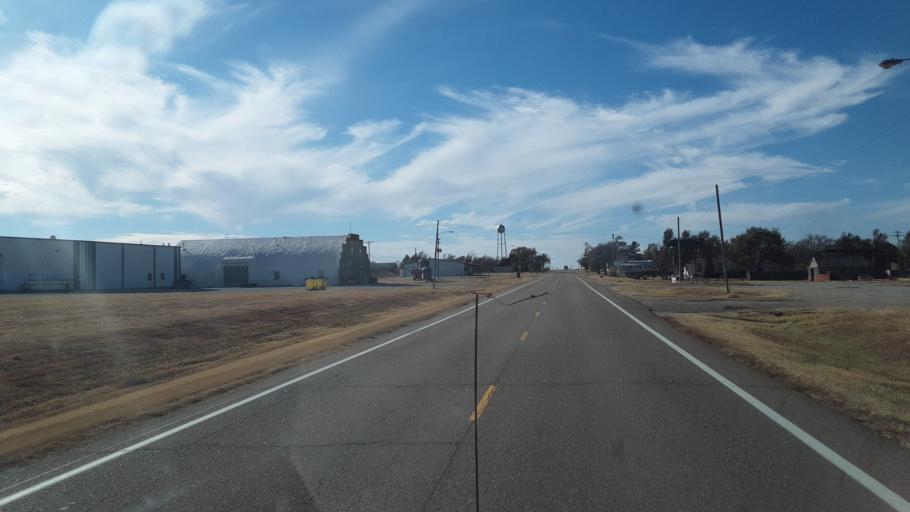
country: US
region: Kansas
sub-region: Edwards County
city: Kinsley
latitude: 38.1897
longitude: -99.5222
